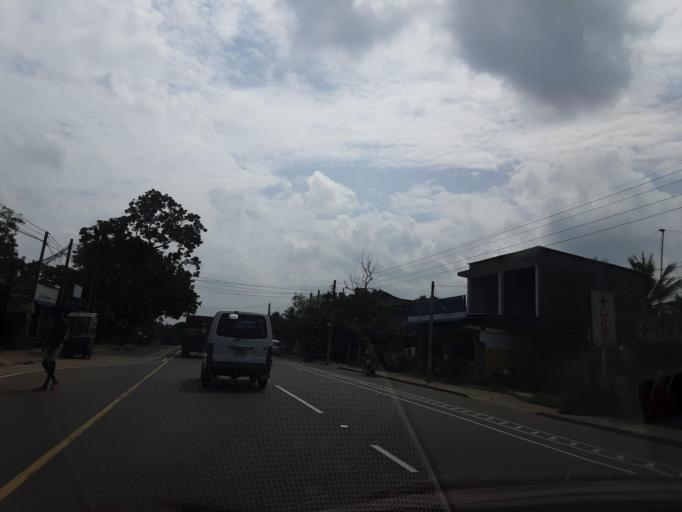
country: LK
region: North Central
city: Anuradhapura
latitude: 8.4702
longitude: 80.5126
